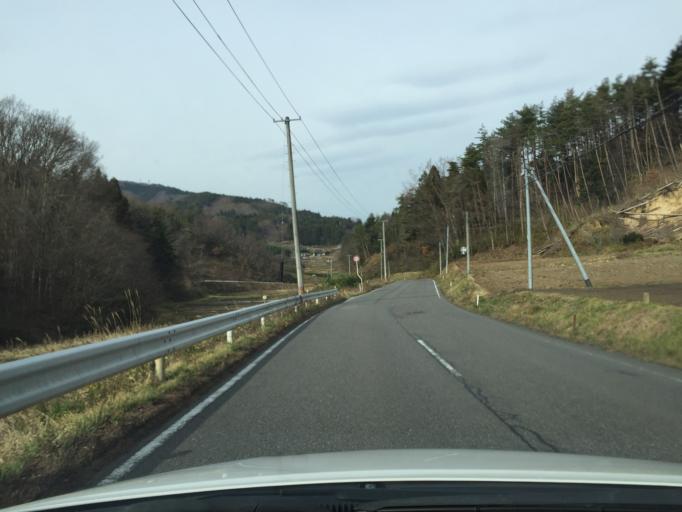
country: JP
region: Fukushima
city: Funehikimachi-funehiki
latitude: 37.4146
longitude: 140.5855
